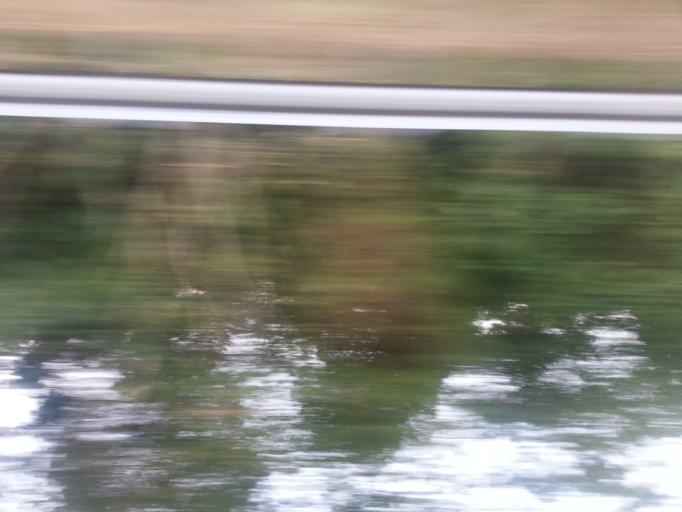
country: US
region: Tennessee
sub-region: Sevier County
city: Seymour
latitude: 35.9291
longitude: -83.8094
